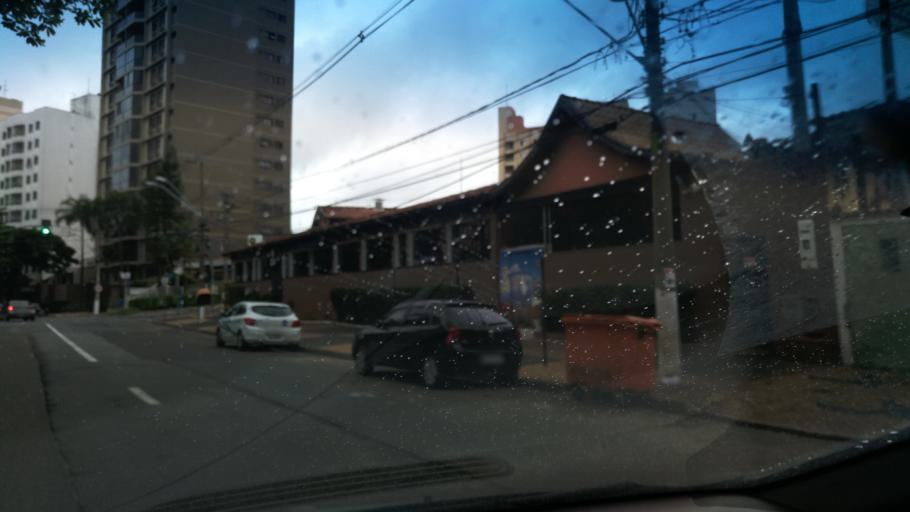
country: BR
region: Sao Paulo
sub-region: Campinas
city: Campinas
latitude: -22.9175
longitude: -47.0438
